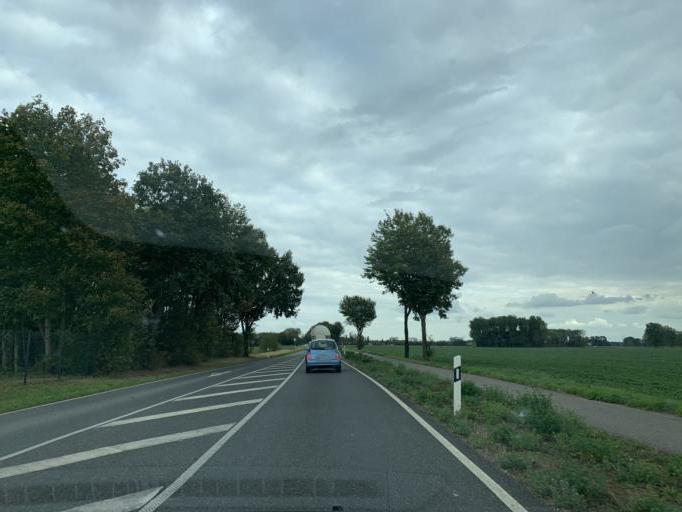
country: DE
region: North Rhine-Westphalia
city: Huckelhoven
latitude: 51.0513
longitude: 6.1850
